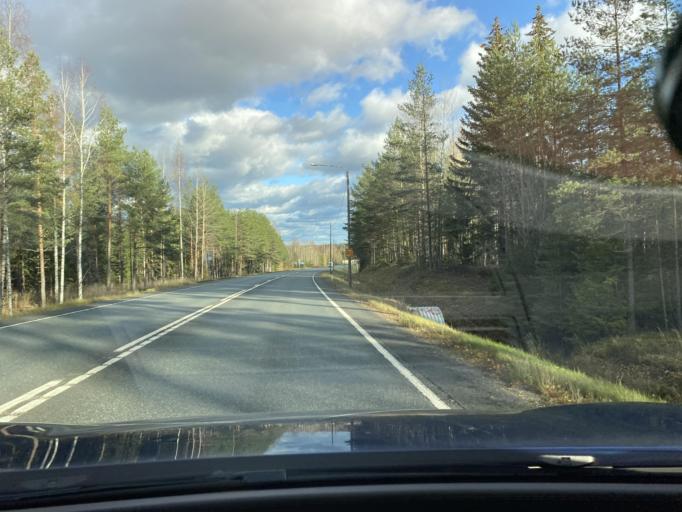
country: FI
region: Haeme
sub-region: Riihimaeki
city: Hausjaervi
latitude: 60.7834
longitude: 24.8915
